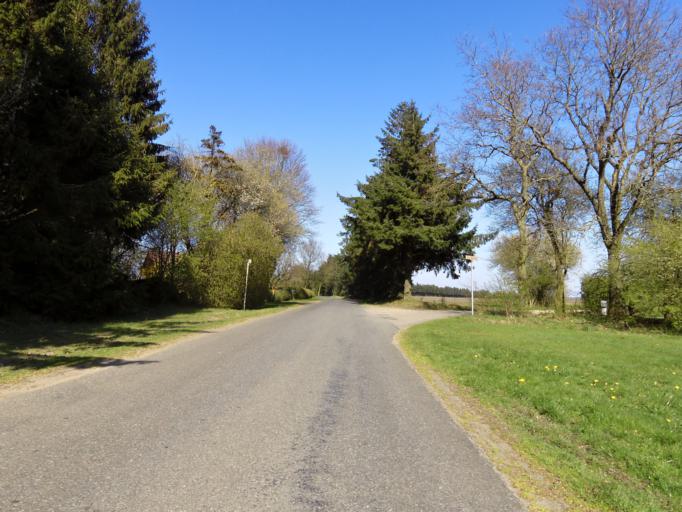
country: DK
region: South Denmark
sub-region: Esbjerg Kommune
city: Ribe
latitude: 55.3569
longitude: 8.7979
